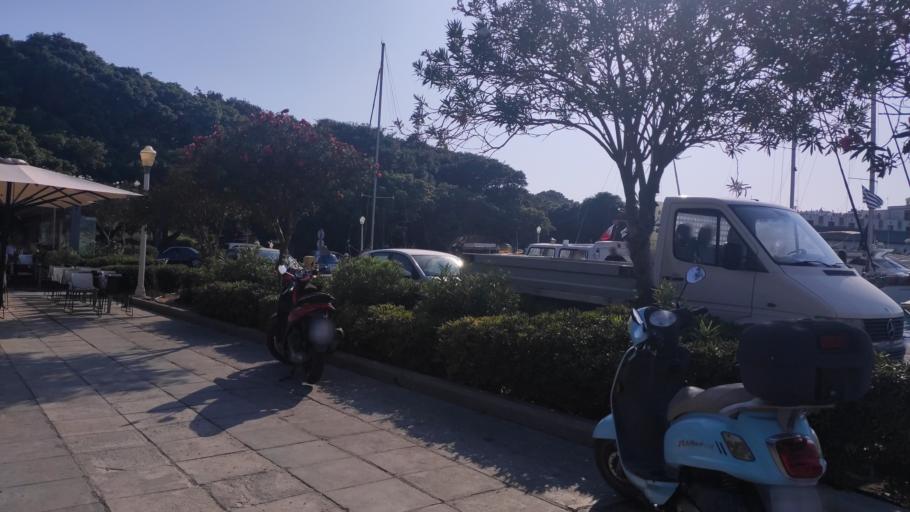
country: GR
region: South Aegean
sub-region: Nomos Dodekanisou
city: Rodos
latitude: 36.4475
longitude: 28.2273
